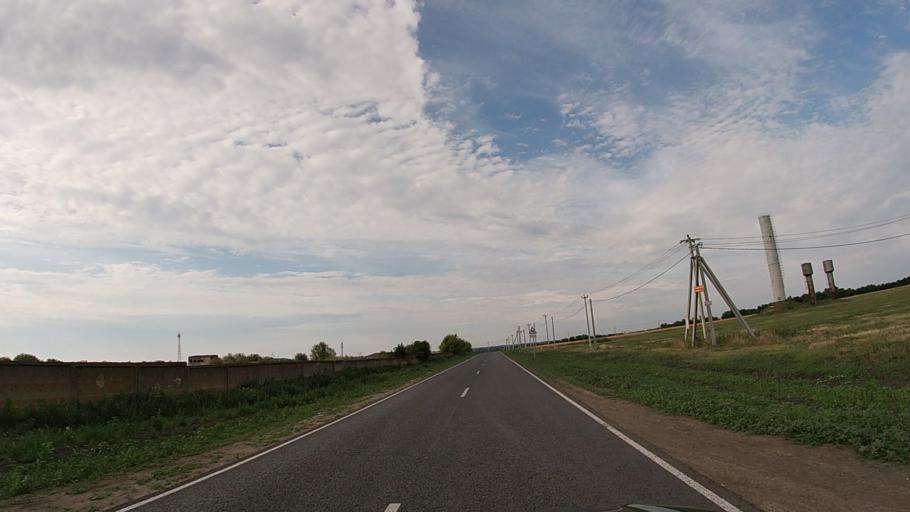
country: RU
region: Belgorod
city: Severnyy
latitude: 50.7243
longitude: 36.5844
